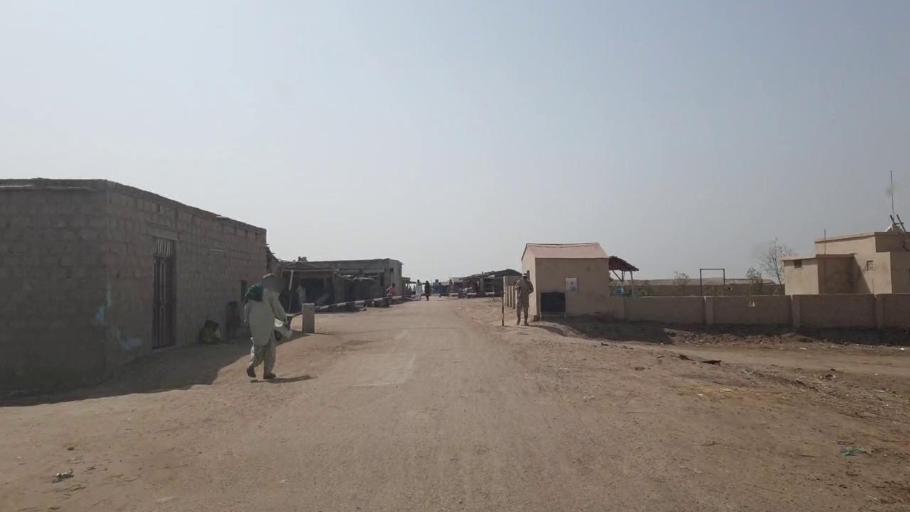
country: PK
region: Sindh
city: Jati
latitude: 24.3365
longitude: 68.5930
